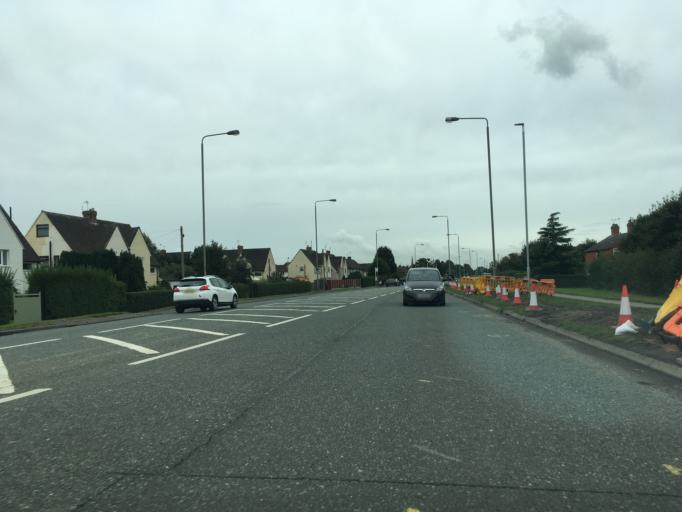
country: GB
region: England
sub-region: Nottinghamshire
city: Newark on Trent
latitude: 53.0902
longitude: -0.7917
